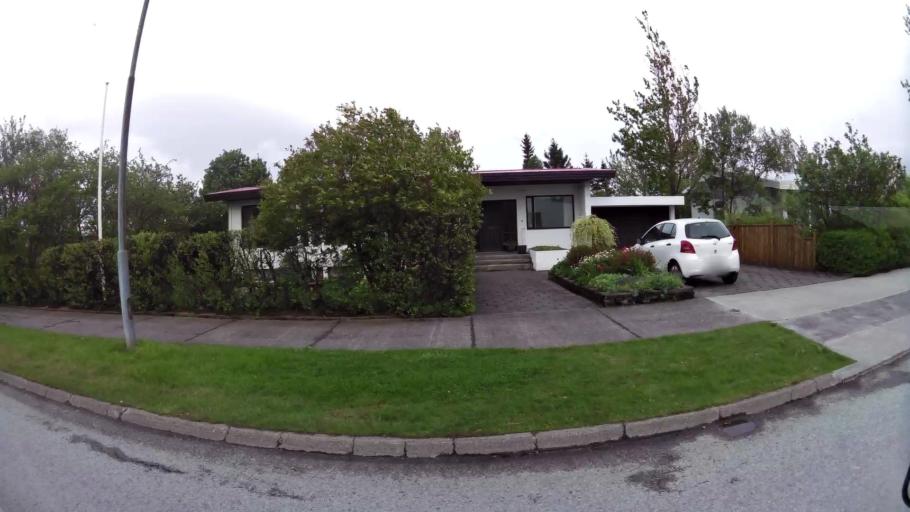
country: IS
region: Capital Region
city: Hafnarfjoerdur
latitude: 64.0784
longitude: -21.9685
